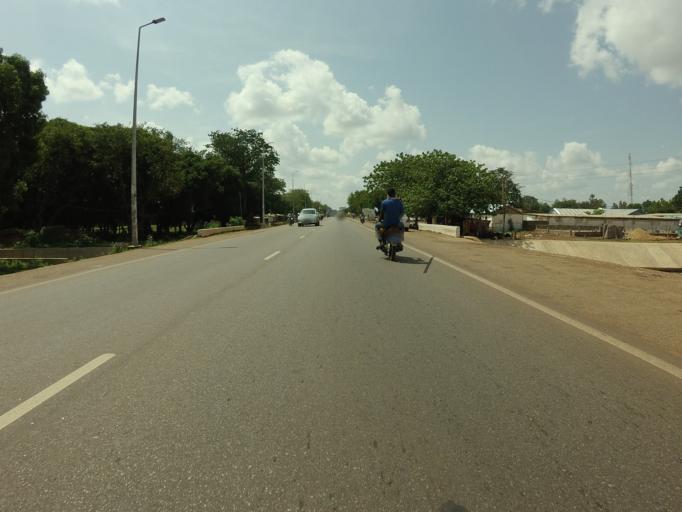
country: GH
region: Northern
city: Tamale
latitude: 9.4450
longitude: -0.8443
